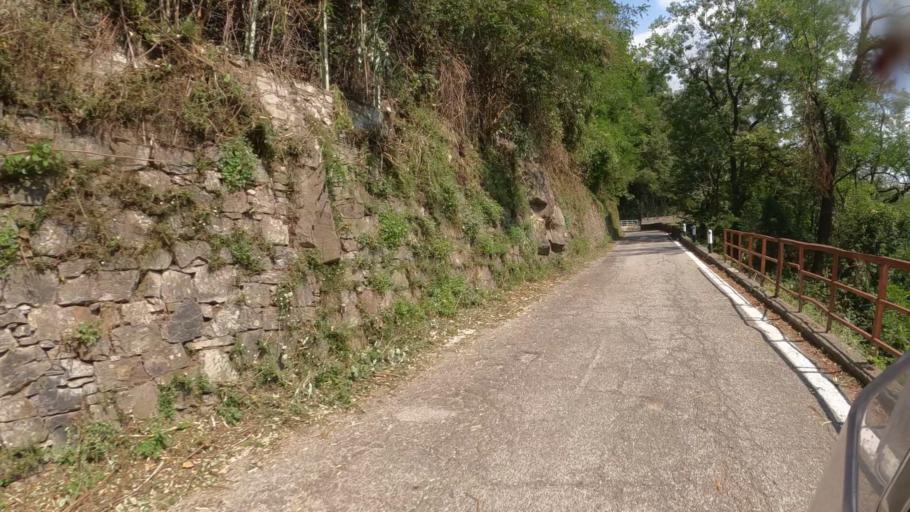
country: IT
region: Lombardy
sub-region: Provincia di Varese
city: Agra
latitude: 46.0573
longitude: 8.7671
